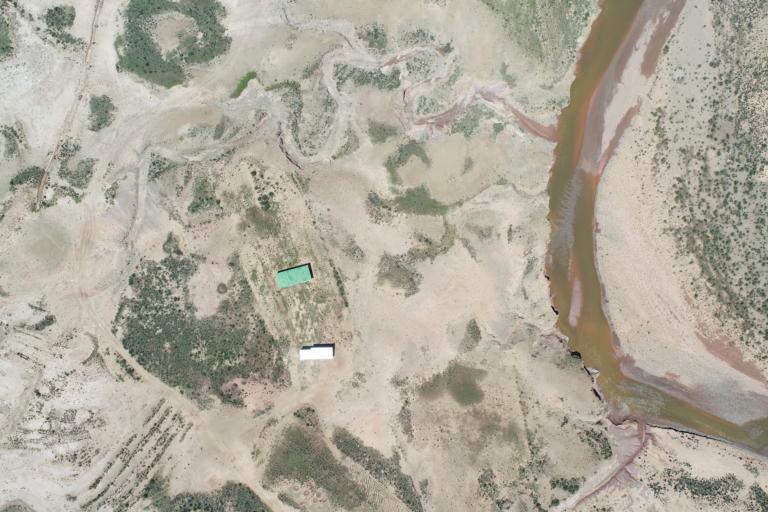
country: BO
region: La Paz
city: Curahuara de Carangas
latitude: -17.3146
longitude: -68.5000
